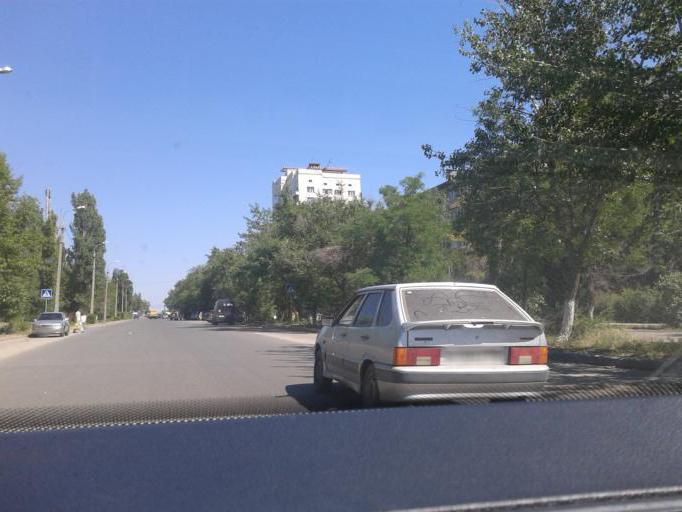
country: RU
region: Volgograd
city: Gorodishche
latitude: 48.7636
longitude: 44.4783
